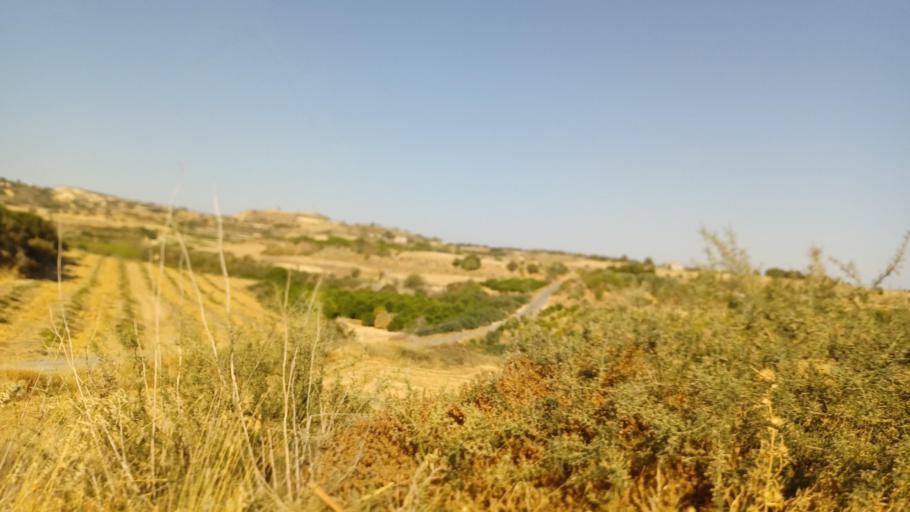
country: CY
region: Pafos
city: Polis
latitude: 35.0181
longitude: 32.4217
